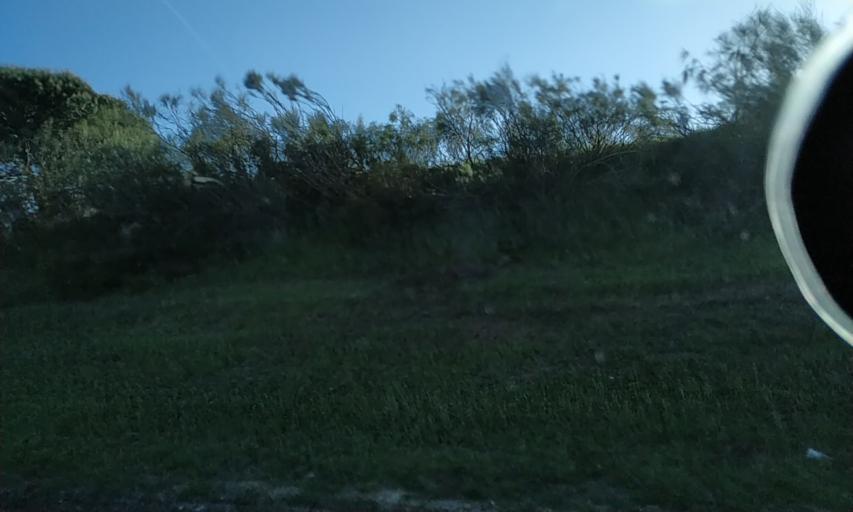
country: PT
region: Lisbon
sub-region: Mafra
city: Milharado
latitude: 38.9511
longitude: -9.2125
